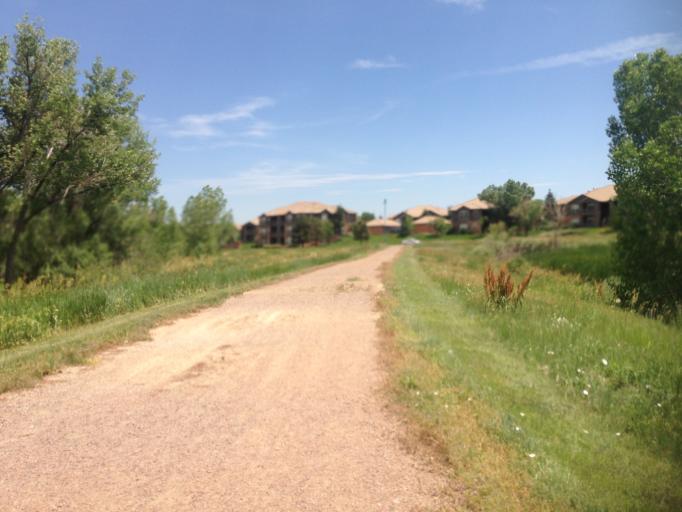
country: US
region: Colorado
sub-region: Boulder County
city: Superior
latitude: 39.9319
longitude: -105.1480
